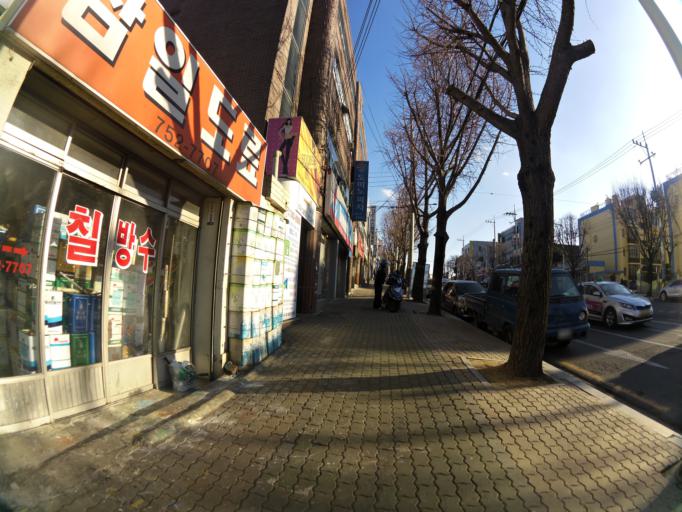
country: KR
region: Daegu
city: Daegu
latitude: 35.8763
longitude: 128.6334
